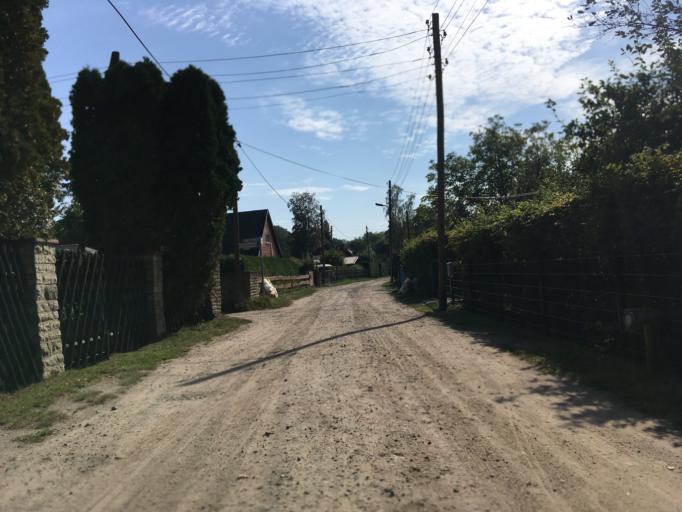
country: DE
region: Berlin
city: Rahnsdorf
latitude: 52.4300
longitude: 13.7108
